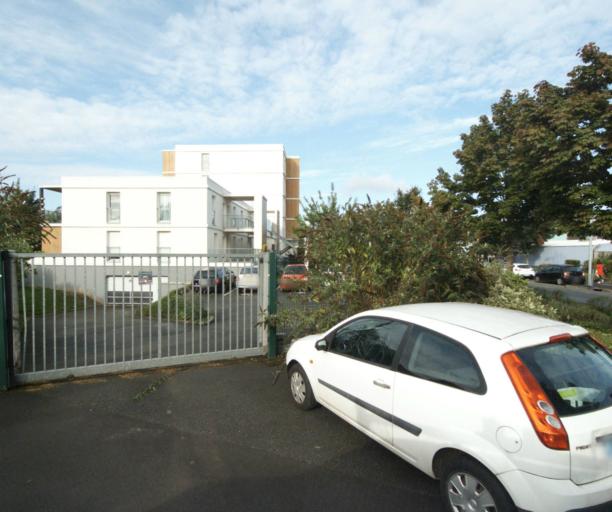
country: FR
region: Nord-Pas-de-Calais
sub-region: Departement du Nord
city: Wattignies
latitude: 50.6029
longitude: 3.0417
